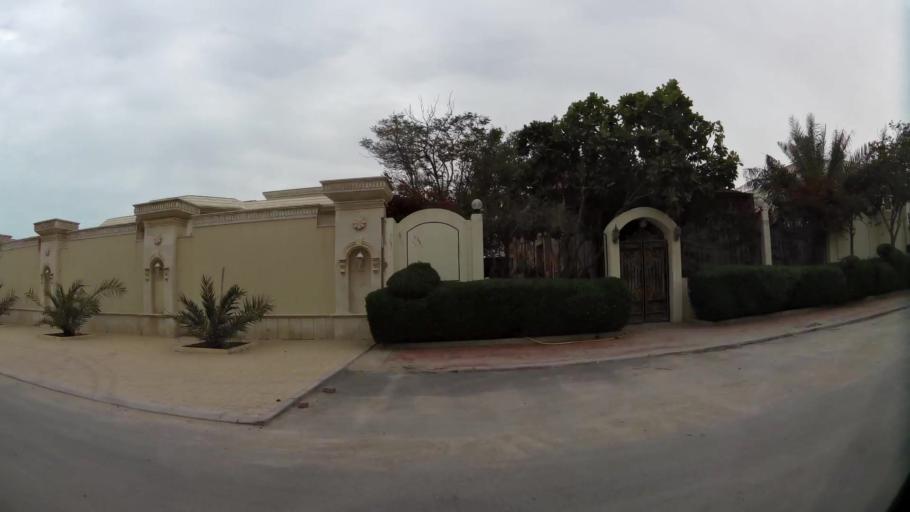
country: QA
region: Baladiyat ar Rayyan
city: Ar Rayyan
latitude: 25.3414
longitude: 51.4616
